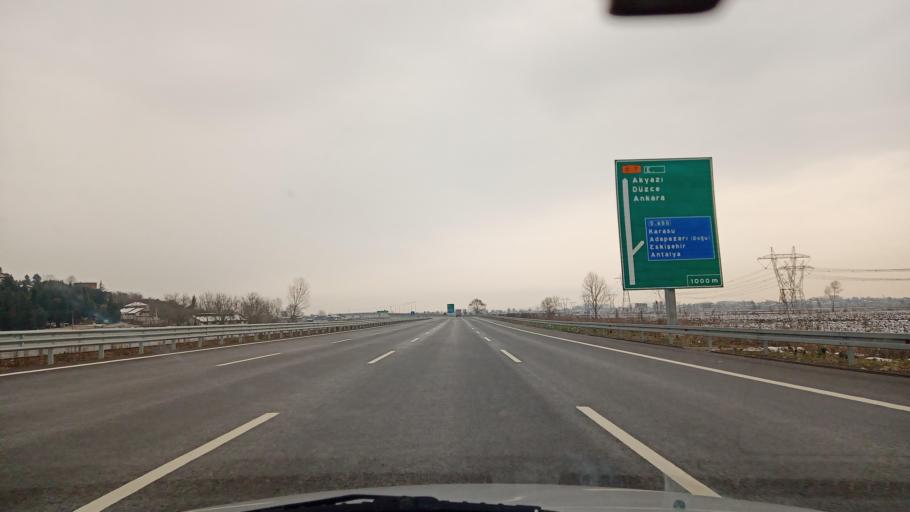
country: TR
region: Sakarya
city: Adapazari
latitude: 40.8192
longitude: 30.4138
